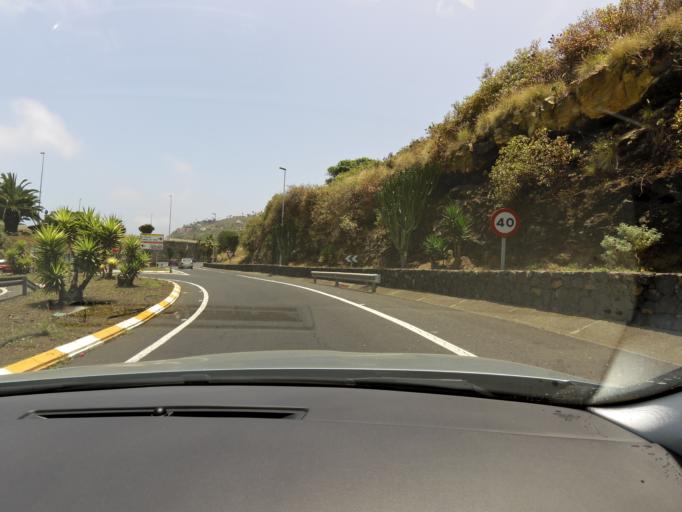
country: ES
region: Canary Islands
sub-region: Provincia de Santa Cruz de Tenerife
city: La Orotava
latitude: 28.4023
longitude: -16.5155
